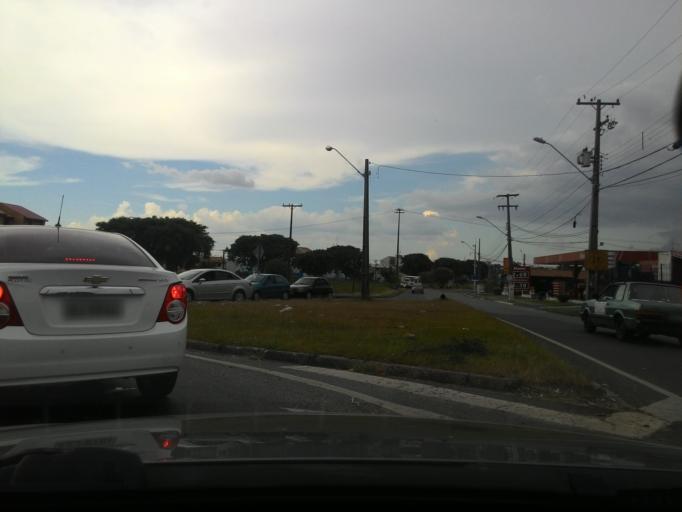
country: BR
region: Parana
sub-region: Pinhais
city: Pinhais
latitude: -25.4439
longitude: -49.2078
